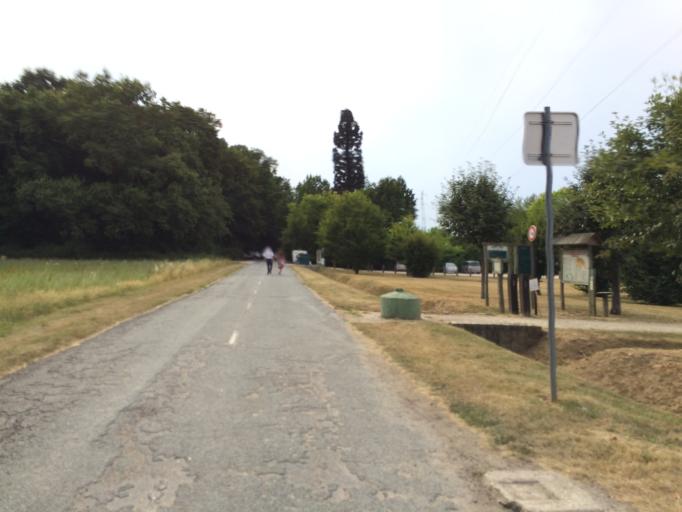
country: FR
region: Ile-de-France
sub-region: Departement de l'Essonne
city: Quincy-sous-Senart
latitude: 48.6599
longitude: 2.5482
